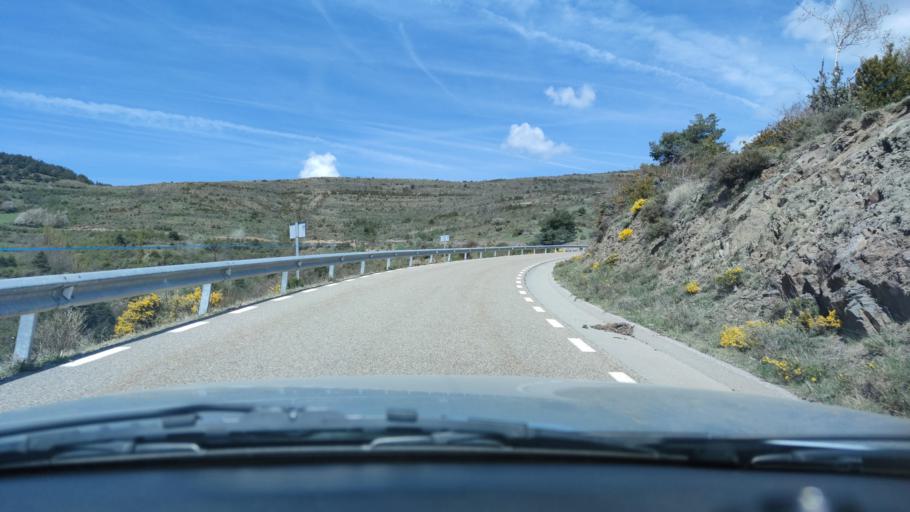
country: ES
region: Catalonia
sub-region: Provincia de Lleida
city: Coll de Nargo
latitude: 42.2935
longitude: 1.2393
